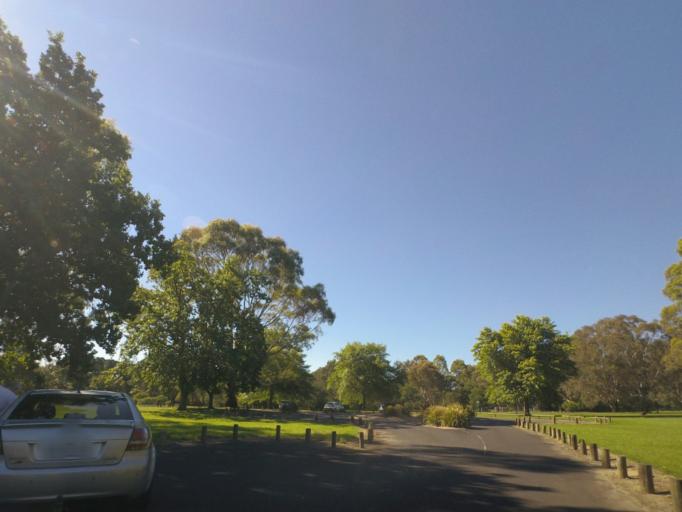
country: AU
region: Victoria
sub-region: Manningham
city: Bulleen
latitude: -37.7563
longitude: 145.0802
